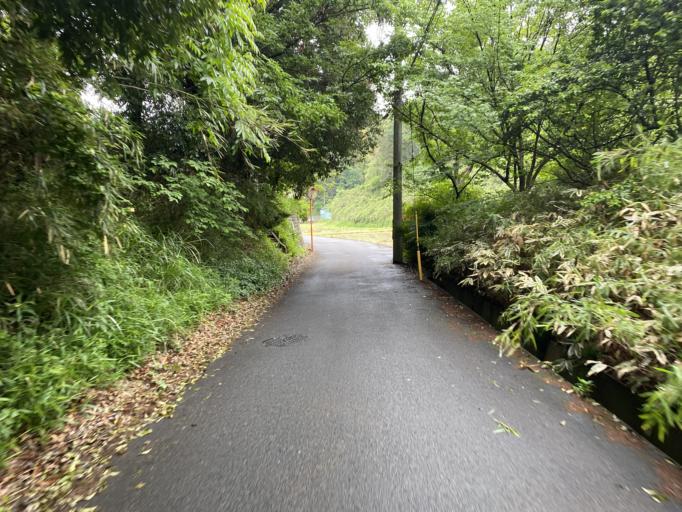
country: JP
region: Tokyo
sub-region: Machida-shi
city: Machida
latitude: 35.5702
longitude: 139.5037
